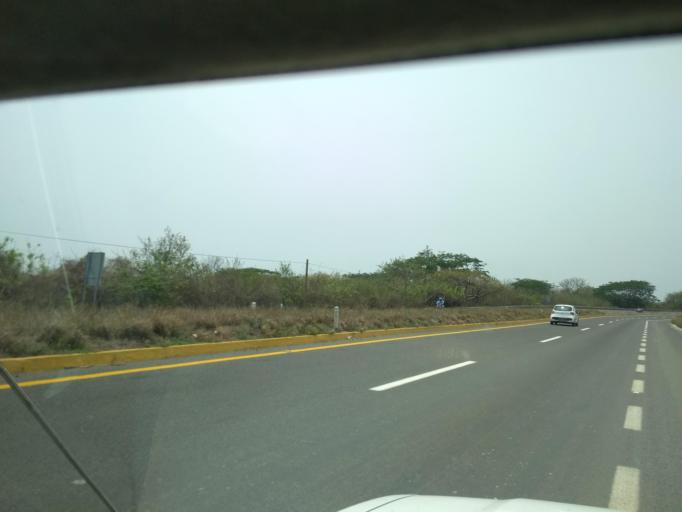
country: MX
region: Veracruz
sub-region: Veracruz
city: Delfino Victoria (Santa Fe)
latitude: 19.2156
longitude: -96.2581
